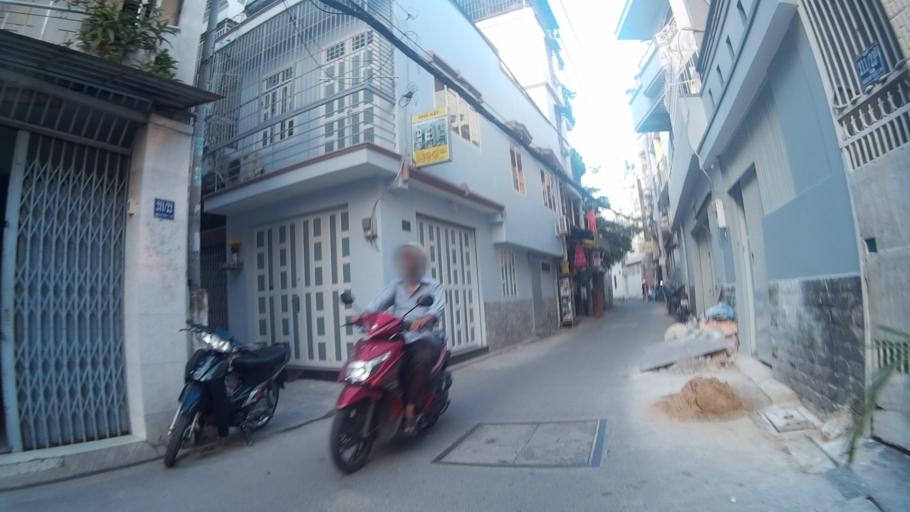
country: VN
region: Ho Chi Minh City
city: Quan Binh Thanh
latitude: 10.8094
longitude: 106.6835
